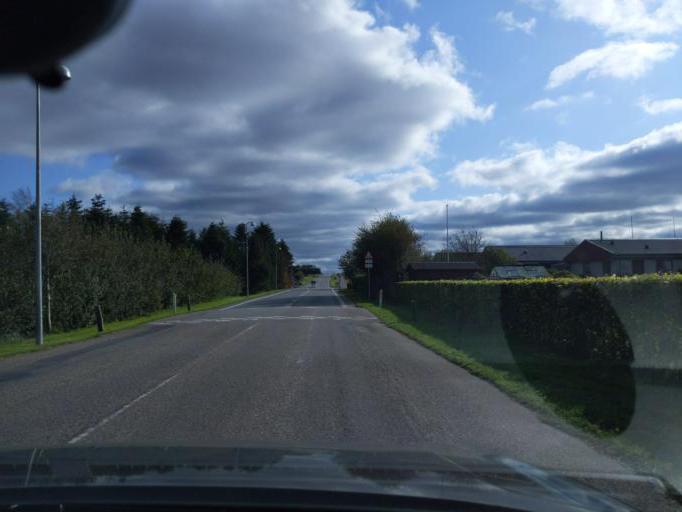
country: DK
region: North Denmark
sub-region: Mariagerfjord Kommune
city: Hobro
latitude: 56.5253
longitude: 9.7295
